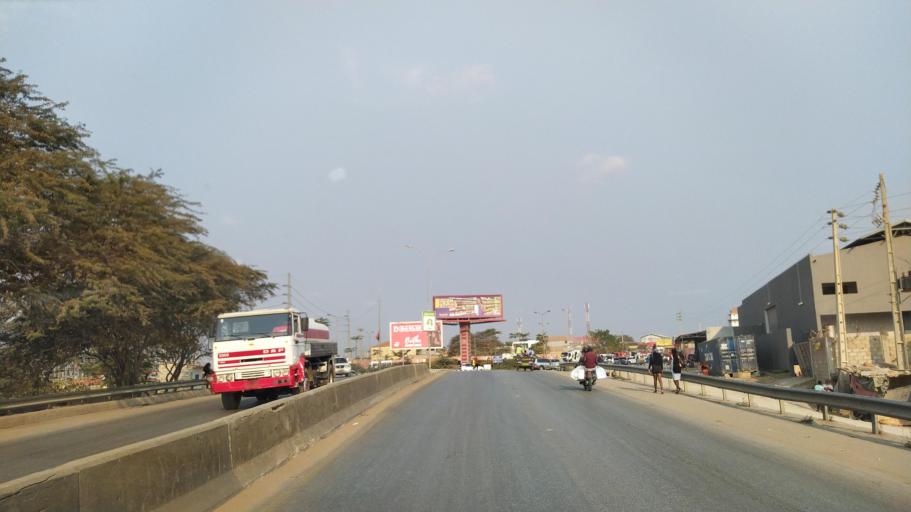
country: AO
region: Luanda
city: Luanda
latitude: -8.9207
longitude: 13.2211
